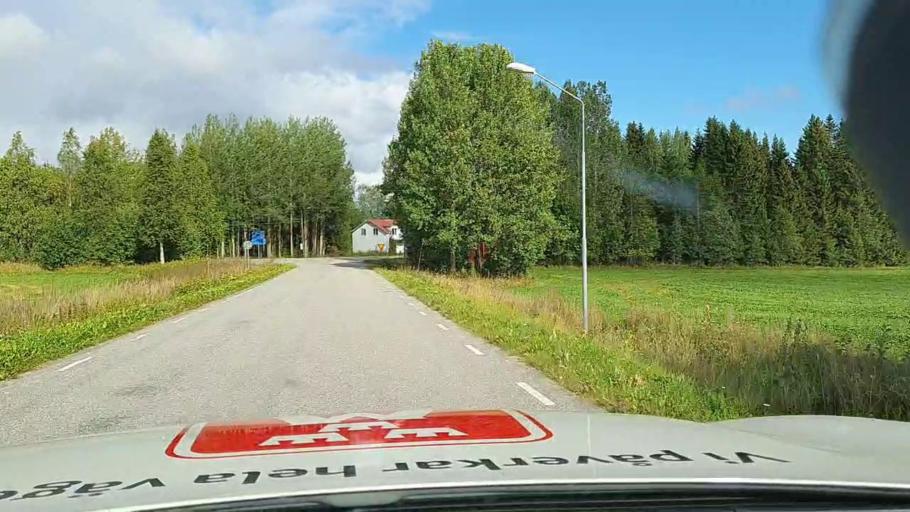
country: SE
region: Jaemtland
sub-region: Stroemsunds Kommun
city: Stroemsund
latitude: 63.8439
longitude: 15.3380
